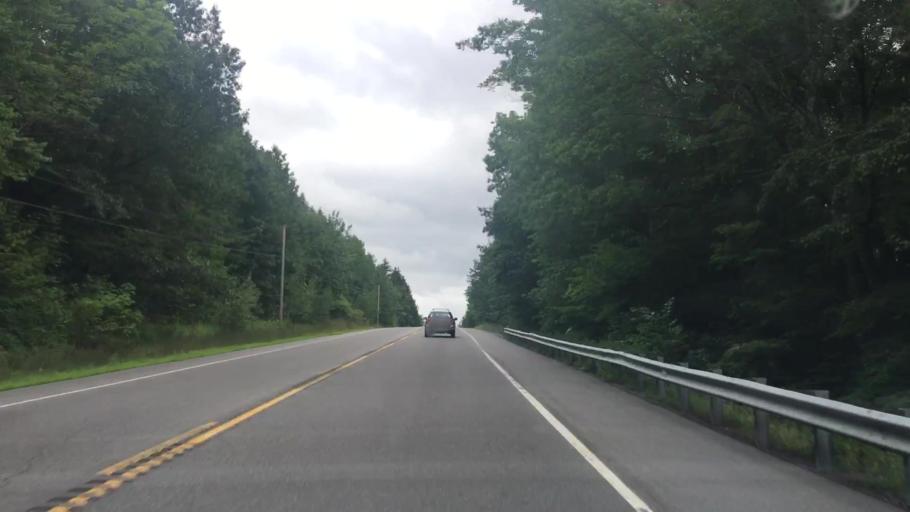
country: US
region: Maine
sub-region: York County
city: Alfred
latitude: 43.5042
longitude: -70.7174
